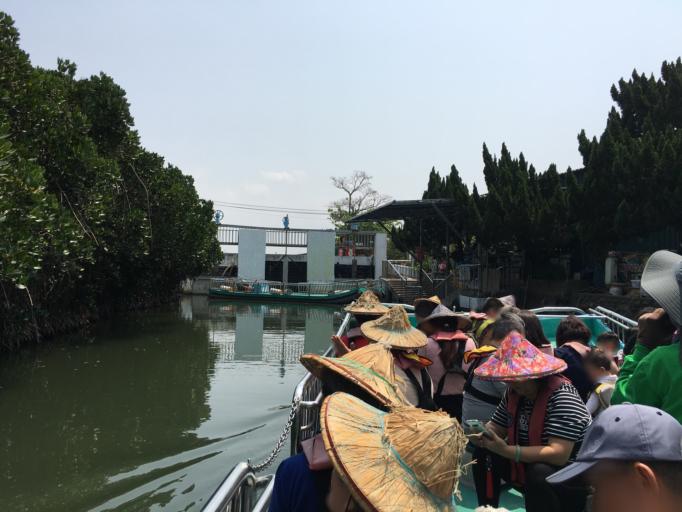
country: TW
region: Taiwan
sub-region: Tainan
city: Tainan
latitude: 23.0197
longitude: 120.1360
